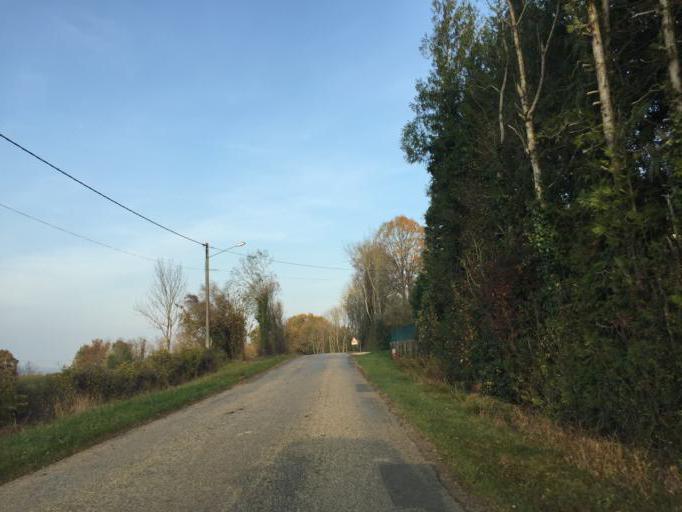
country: FR
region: Rhone-Alpes
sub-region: Departement de l'Ain
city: Chatillon-la-Palud
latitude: 45.9373
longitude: 5.2388
